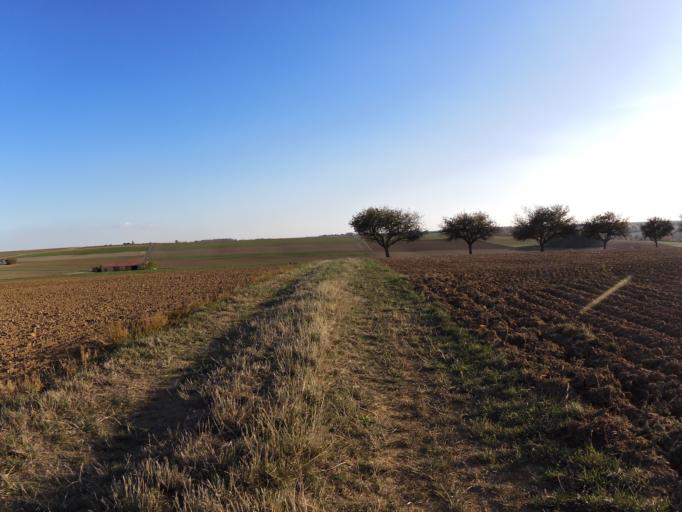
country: DE
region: Bavaria
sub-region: Regierungsbezirk Unterfranken
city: Reichenberg
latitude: 49.7286
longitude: 9.9266
